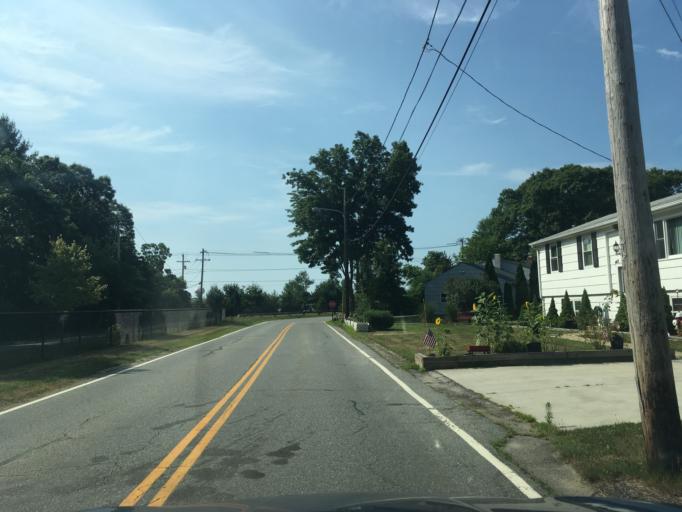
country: US
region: Rhode Island
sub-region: Kent County
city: East Greenwich
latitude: 41.6107
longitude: -71.4349
